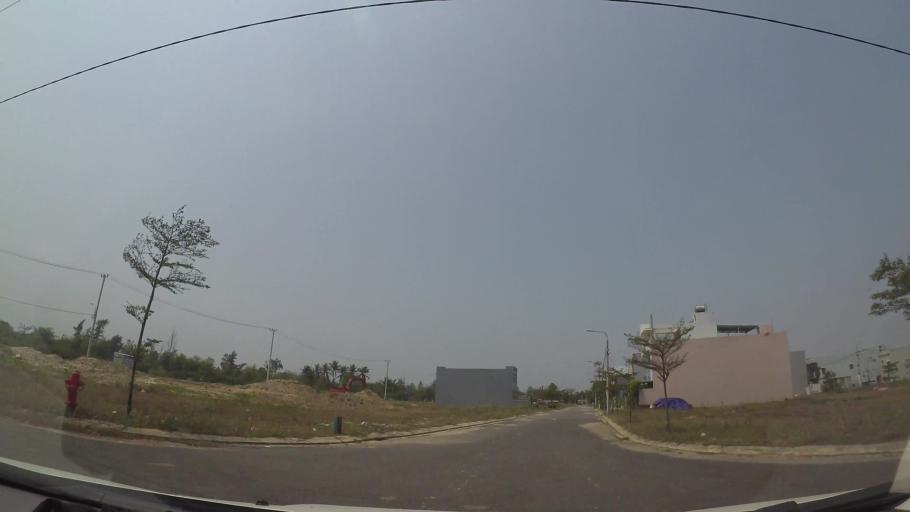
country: VN
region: Da Nang
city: Ngu Hanh Son
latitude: 15.9846
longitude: 108.2608
